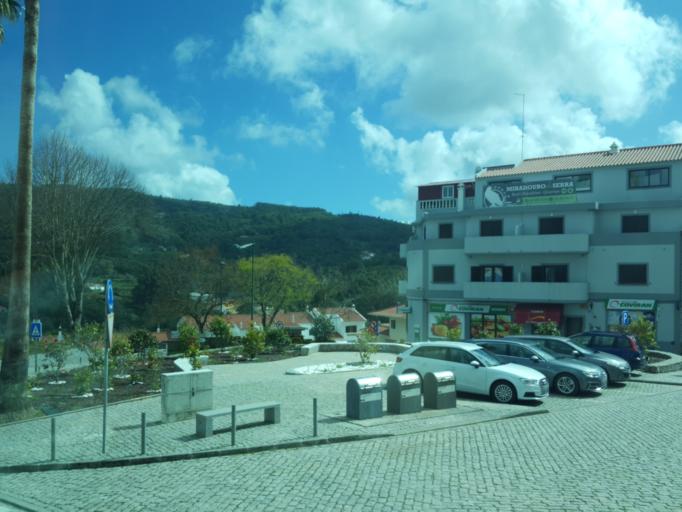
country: PT
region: Faro
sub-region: Monchique
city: Monchique
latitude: 37.3162
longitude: -8.5558
